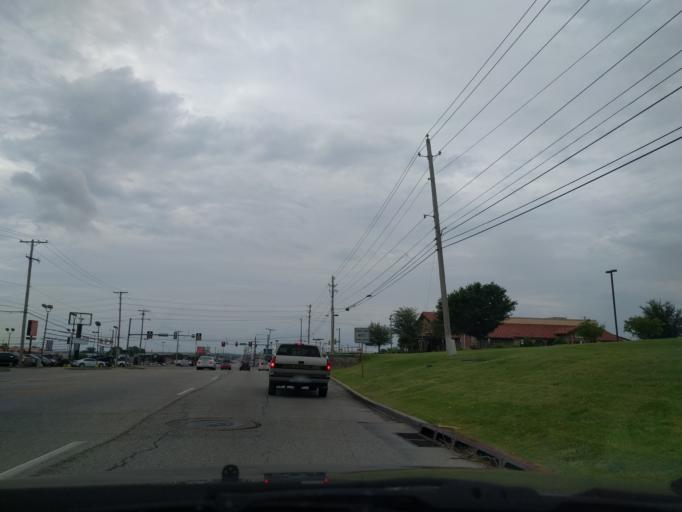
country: US
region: Oklahoma
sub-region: Tulsa County
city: Tulsa
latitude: 36.1043
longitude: -95.9060
